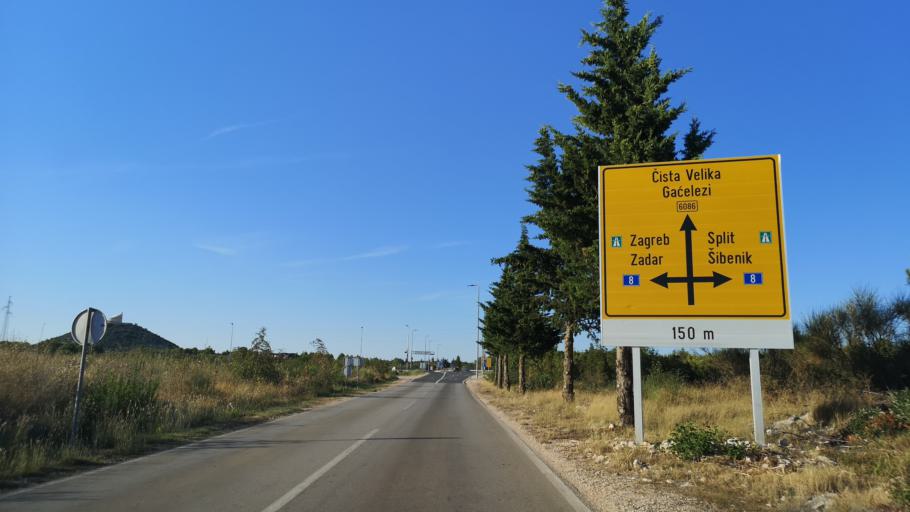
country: HR
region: Sibensko-Kniniska
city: Vodice
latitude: 43.7735
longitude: 15.7727
